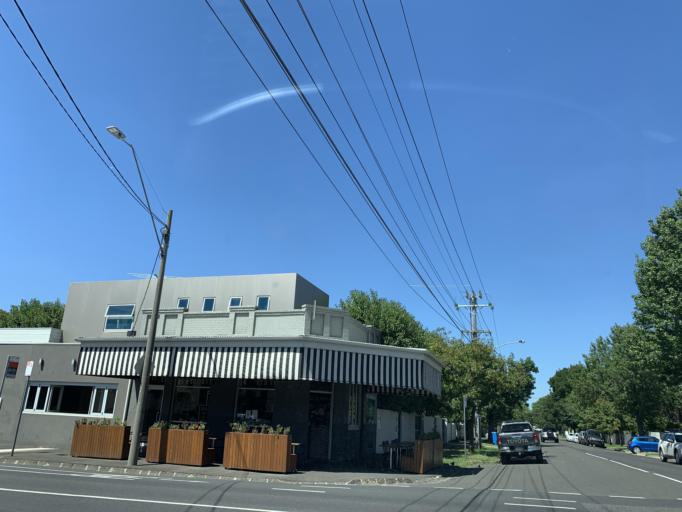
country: AU
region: Victoria
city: Ripponlea
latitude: -37.8942
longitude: 144.9950
